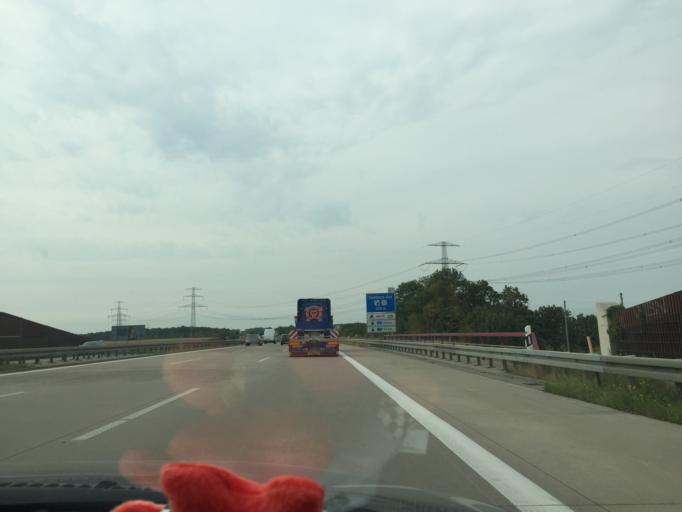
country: DE
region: Brandenburg
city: Neuenhagen
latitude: 52.5373
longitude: 13.7002
